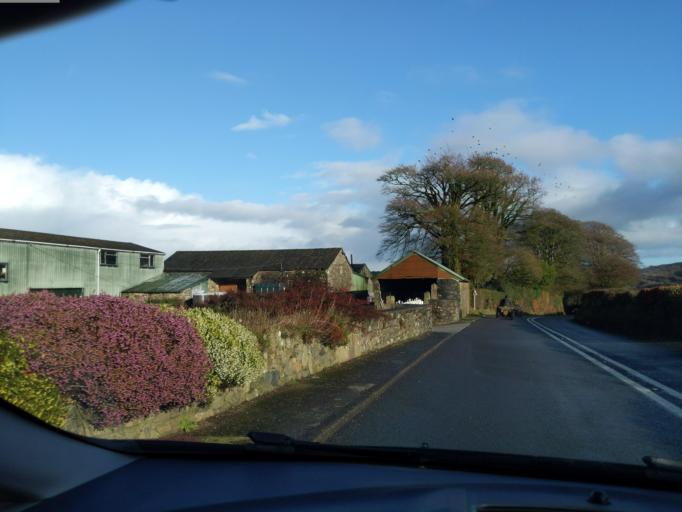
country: GB
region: England
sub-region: Devon
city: Okehampton
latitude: 50.7193
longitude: -4.0413
